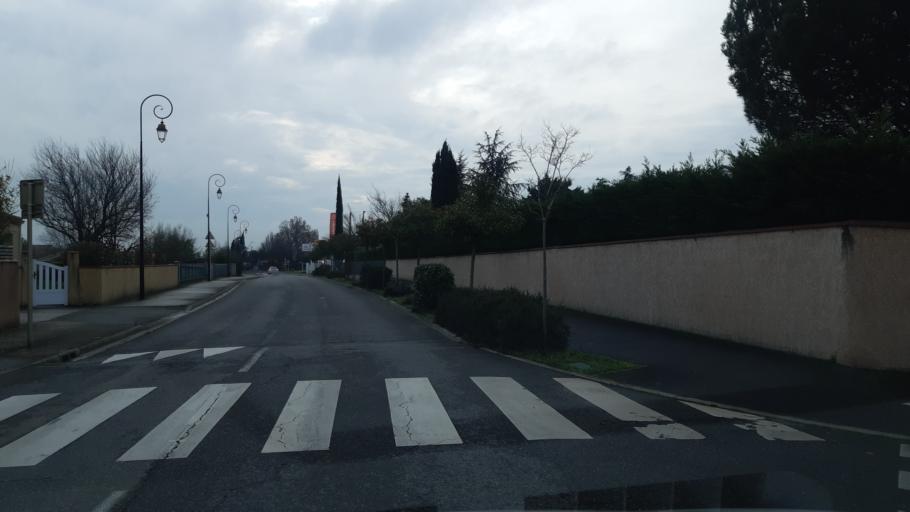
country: FR
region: Midi-Pyrenees
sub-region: Departement de la Haute-Garonne
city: Pibrac
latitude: 43.6118
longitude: 1.2852
